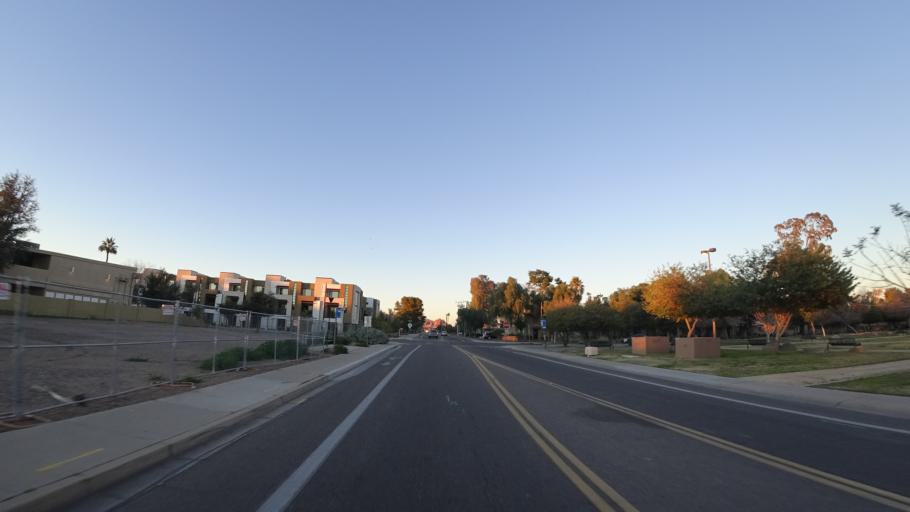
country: US
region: Arizona
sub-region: Maricopa County
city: Tempe Junction
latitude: 33.4250
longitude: -111.9523
